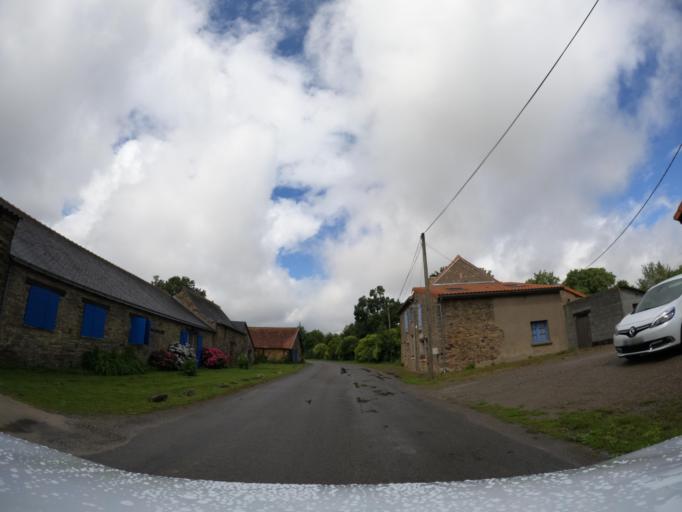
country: FR
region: Pays de la Loire
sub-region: Departement de la Loire-Atlantique
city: Ligne
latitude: 47.3977
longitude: -1.3853
